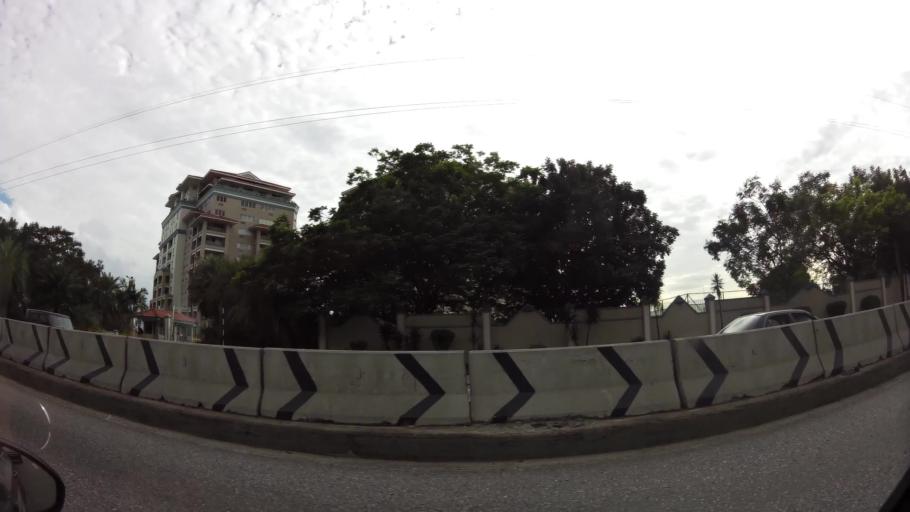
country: TT
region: City of Port of Spain
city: Mucurapo
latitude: 10.6769
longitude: -61.5464
